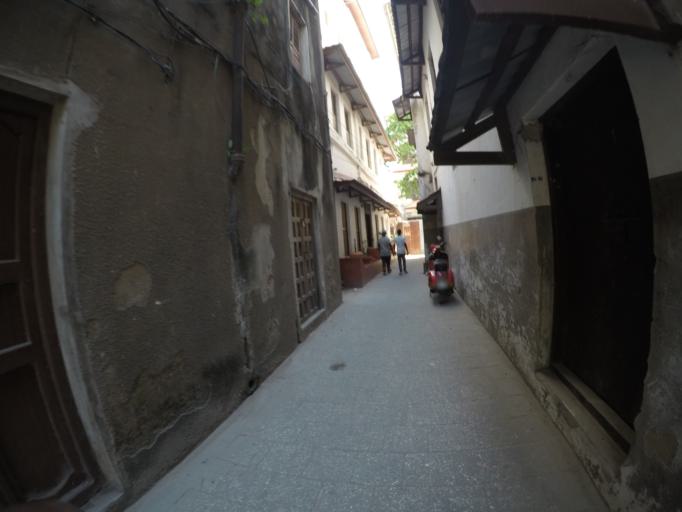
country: TZ
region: Zanzibar Urban/West
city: Zanzibar
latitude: -6.1593
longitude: 39.1939
